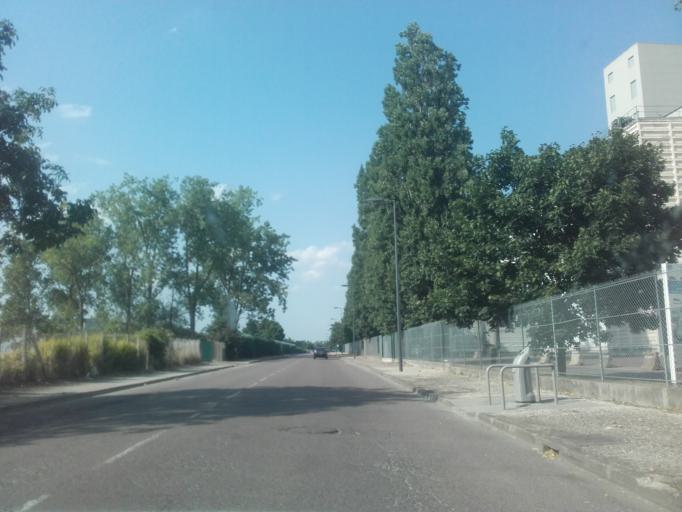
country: FR
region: Bourgogne
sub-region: Departement de la Cote-d'Or
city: Beaune
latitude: 47.0188
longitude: 4.8638
